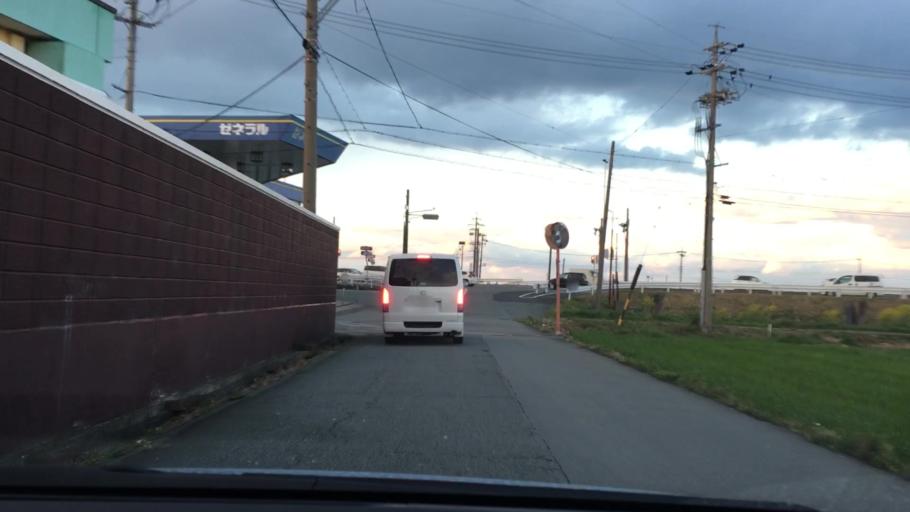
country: JP
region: Mie
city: Ise
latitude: 34.5339
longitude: 136.6785
